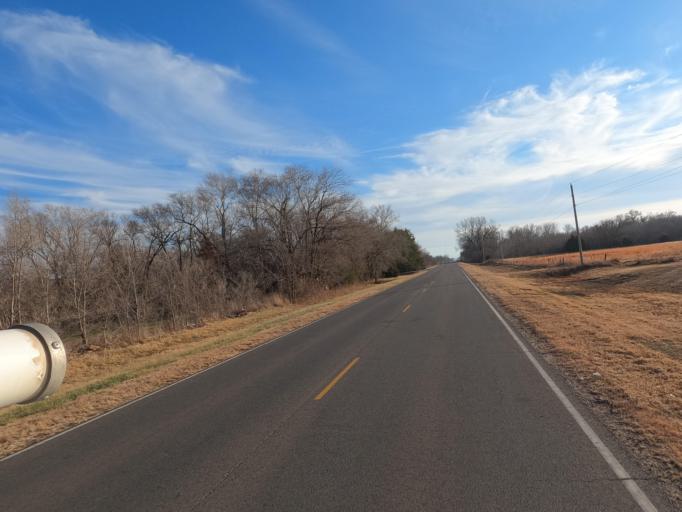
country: US
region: Kansas
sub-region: Reno County
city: Buhler
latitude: 38.1235
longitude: -97.7754
